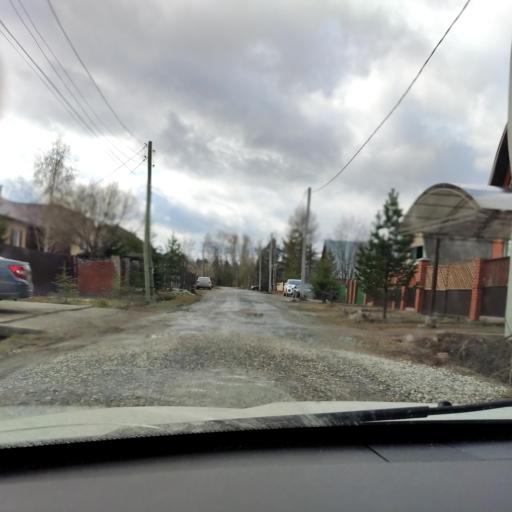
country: RU
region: Perm
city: Polazna
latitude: 58.1176
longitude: 56.4115
